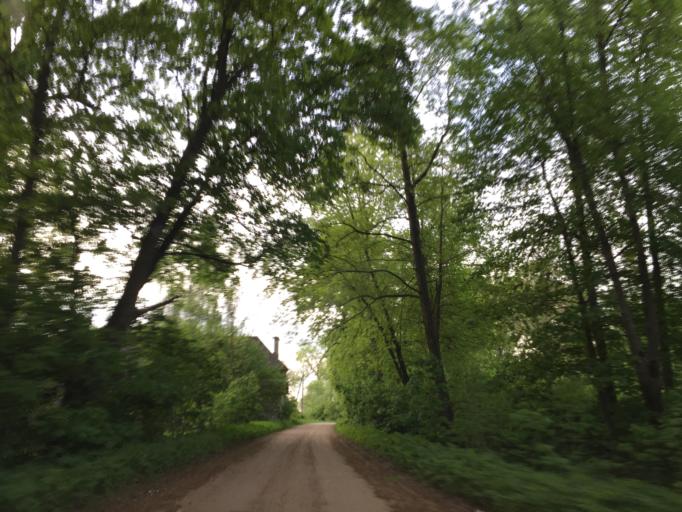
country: LV
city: Tireli
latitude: 56.7162
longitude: 23.4958
